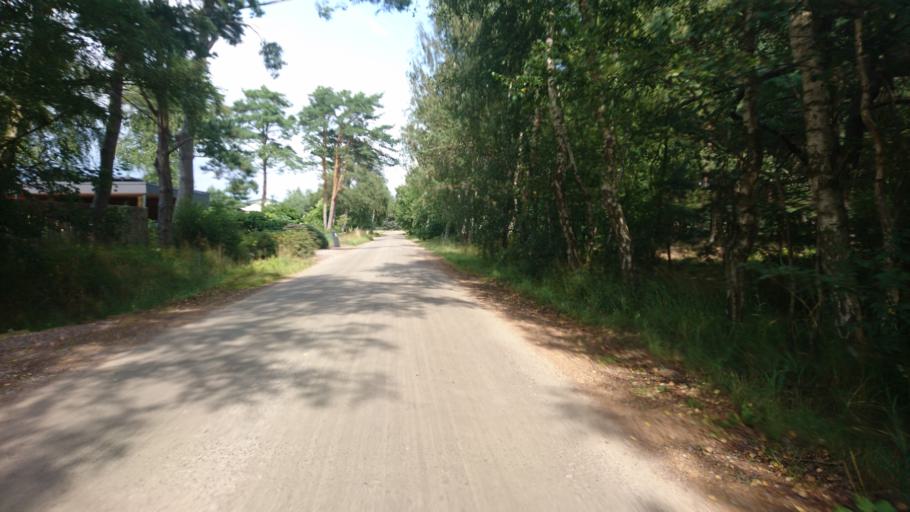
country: SE
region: Skane
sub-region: Vellinge Kommun
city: Ljunghusen
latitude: 55.3985
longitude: 12.9103
